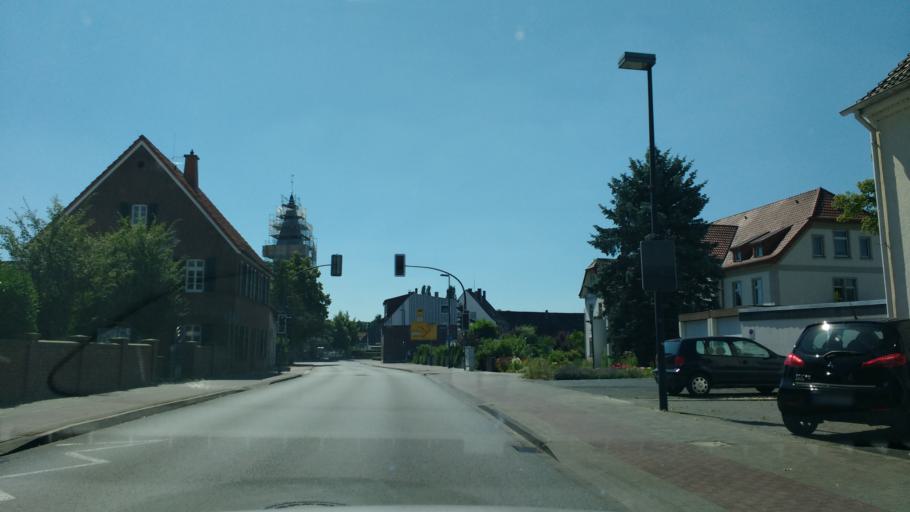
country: DE
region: North Rhine-Westphalia
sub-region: Regierungsbezirk Arnsberg
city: Lippstadt
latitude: 51.6933
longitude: 8.3763
